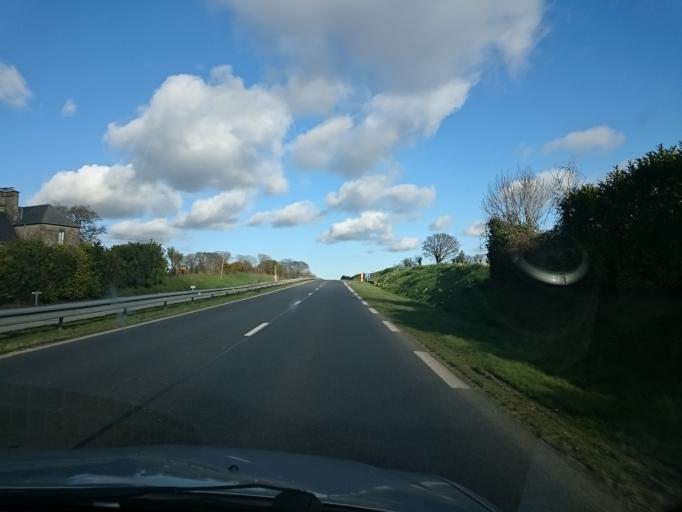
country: FR
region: Lower Normandy
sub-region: Departement de la Manche
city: Valognes
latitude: 49.4964
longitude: -1.4295
